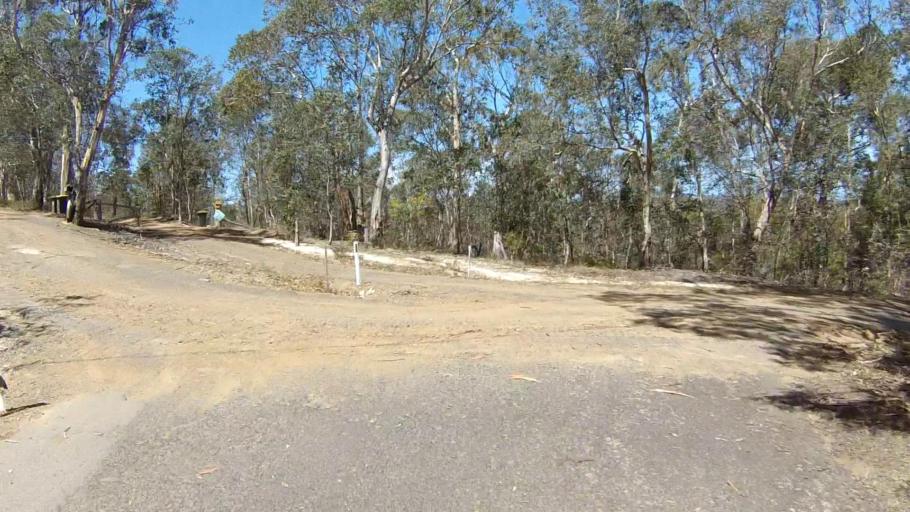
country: AU
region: Tasmania
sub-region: Clarence
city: Sandford
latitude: -42.9745
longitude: 147.4854
